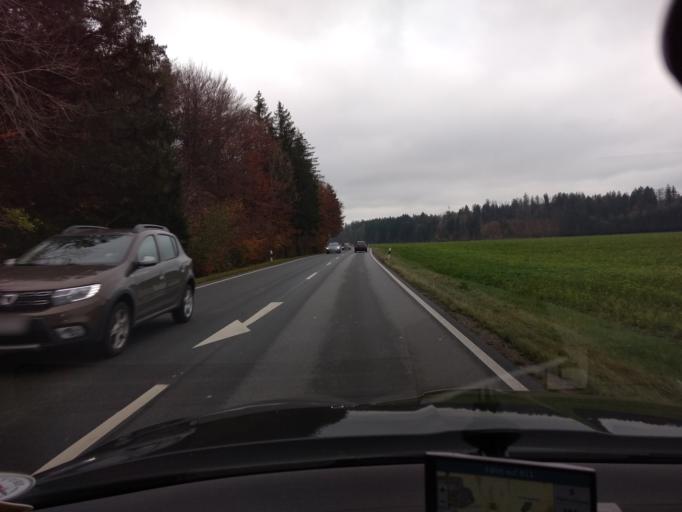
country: DE
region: Bavaria
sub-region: Upper Bavaria
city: Geretsried
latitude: 47.8690
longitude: 11.4698
